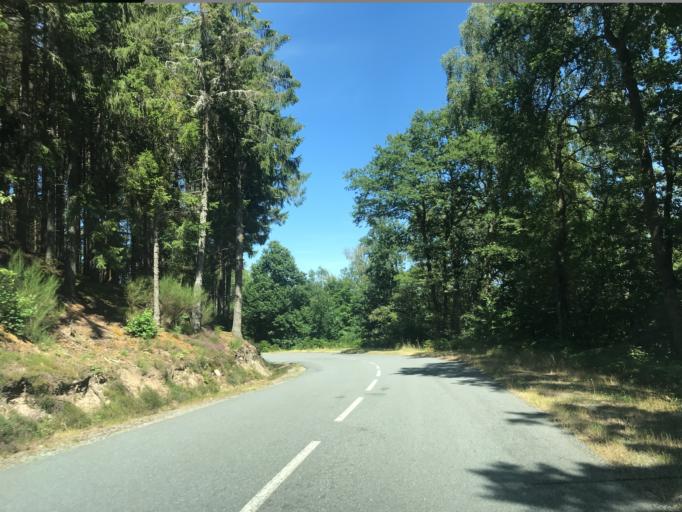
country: FR
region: Limousin
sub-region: Departement de la Creuse
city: Felletin
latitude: 45.7860
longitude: 2.1484
